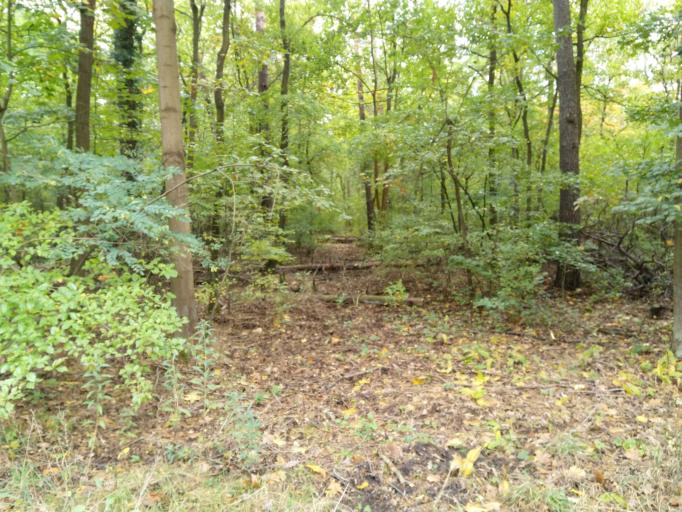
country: DE
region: Berlin
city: Rahnsdorf
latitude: 52.4515
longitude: 13.6828
